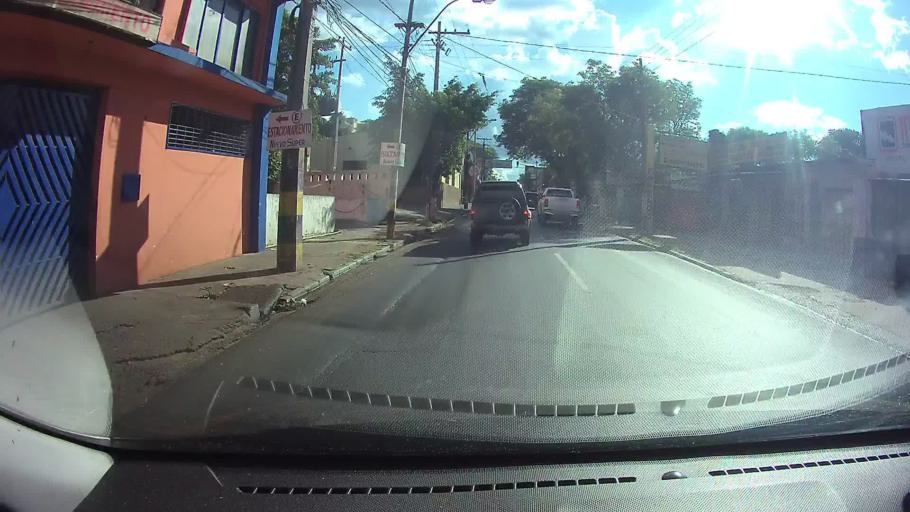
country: PY
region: Cordillera
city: Caacupe
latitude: -25.3845
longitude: -57.1406
